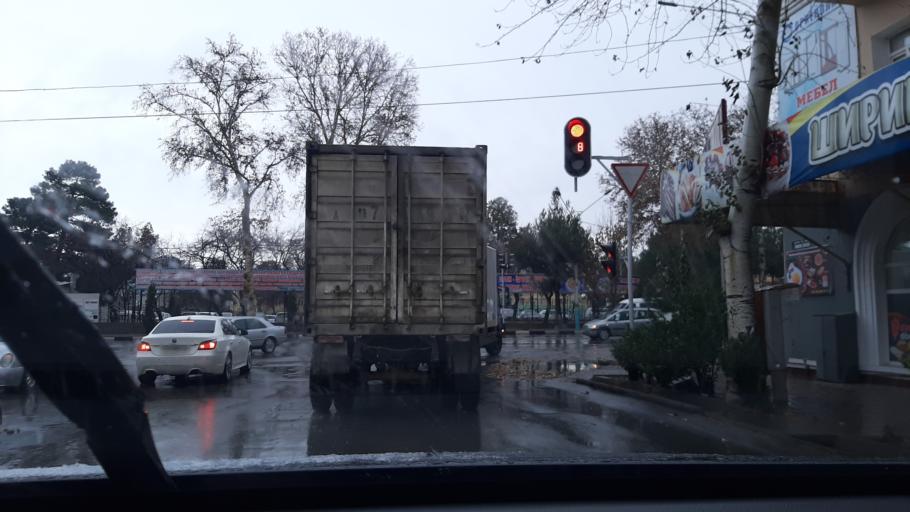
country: TJ
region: Viloyati Sughd
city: Khujand
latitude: 40.2733
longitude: 69.6390
